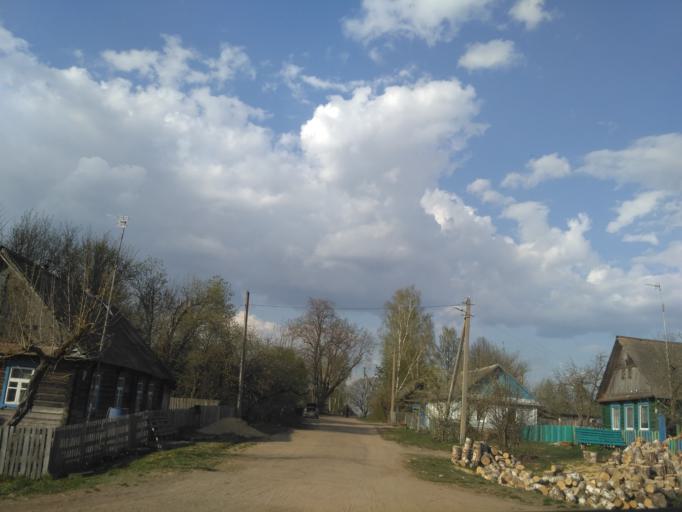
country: BY
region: Minsk
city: Khalopyenichy
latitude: 54.5047
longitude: 28.8497
